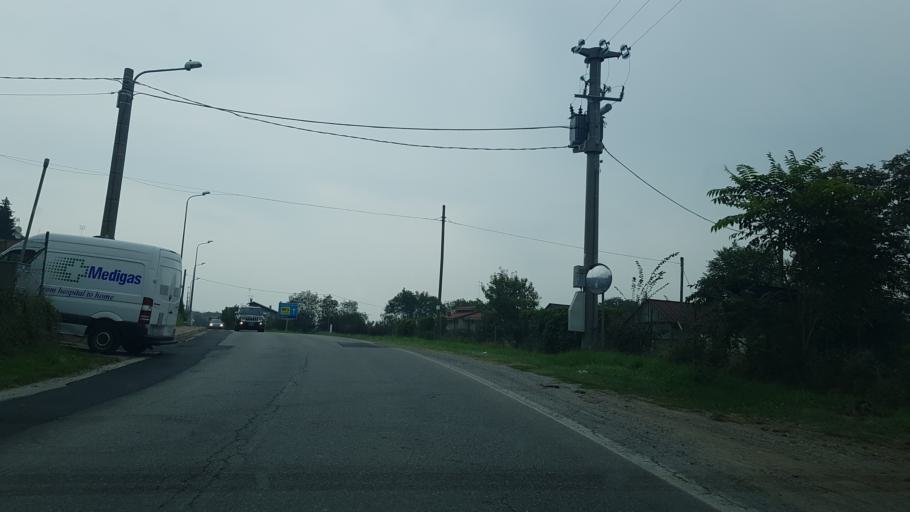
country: IT
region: Piedmont
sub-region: Provincia di Cuneo
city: Villanova Mondovi
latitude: 44.3366
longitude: 7.7602
